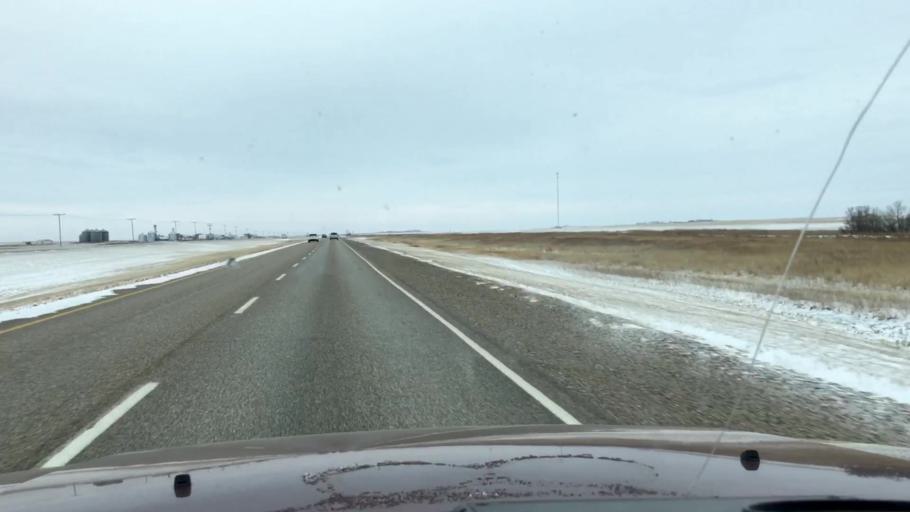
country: CA
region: Saskatchewan
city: Moose Jaw
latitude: 51.0197
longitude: -105.7857
